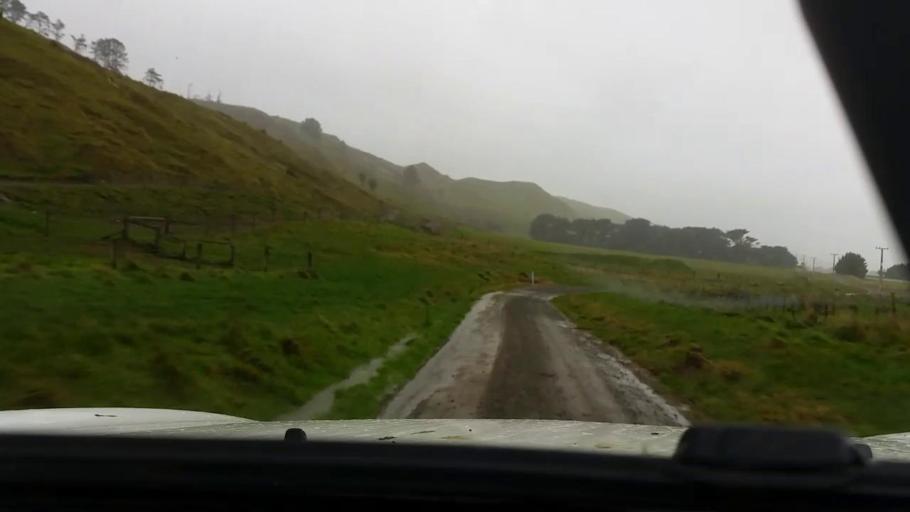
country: NZ
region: Wellington
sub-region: Masterton District
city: Masterton
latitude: -41.2600
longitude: 175.8976
